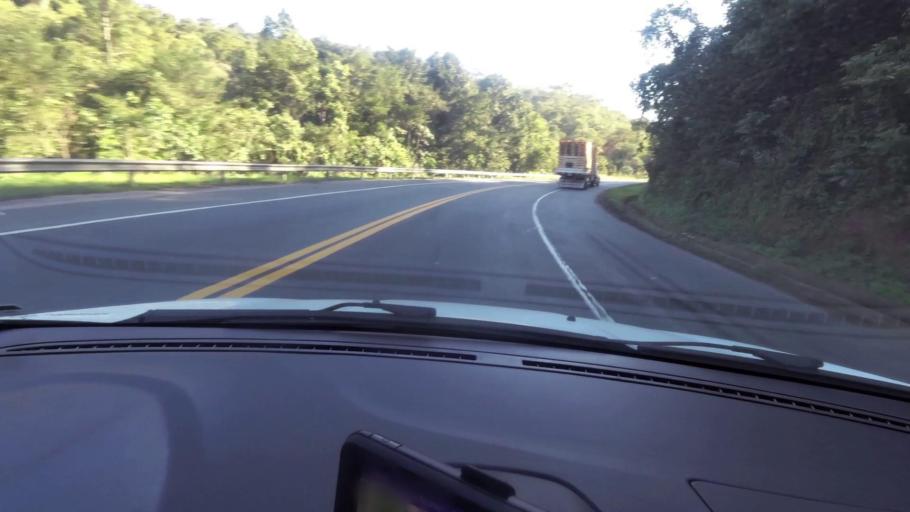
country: BR
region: Espirito Santo
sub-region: Alfredo Chaves
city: Alfredo Chaves
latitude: -20.6655
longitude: -40.6550
